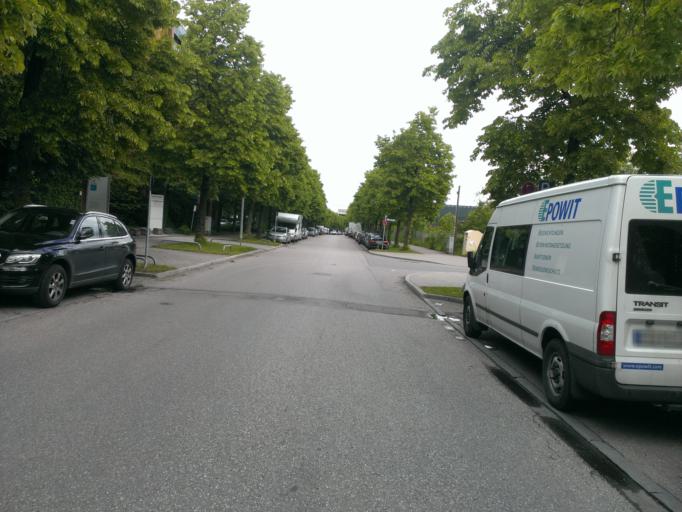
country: DE
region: Bavaria
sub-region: Upper Bavaria
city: Munich
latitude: 48.1788
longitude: 11.5321
